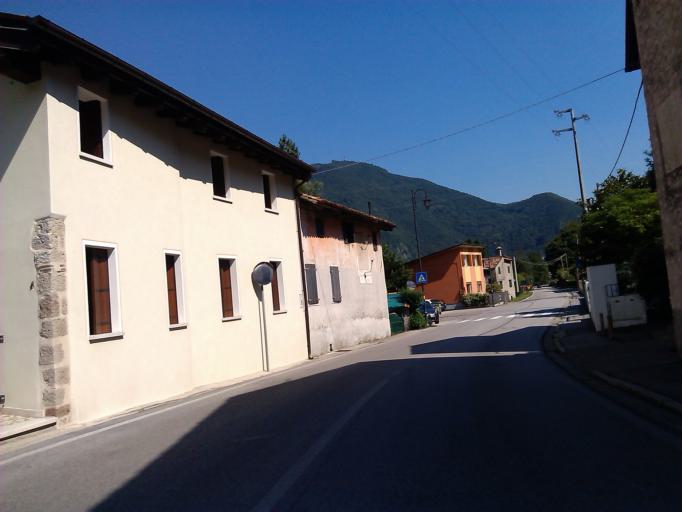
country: IT
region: Veneto
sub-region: Provincia di Vicenza
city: Campolongo sul Brenta
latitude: 45.8268
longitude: 11.7026
